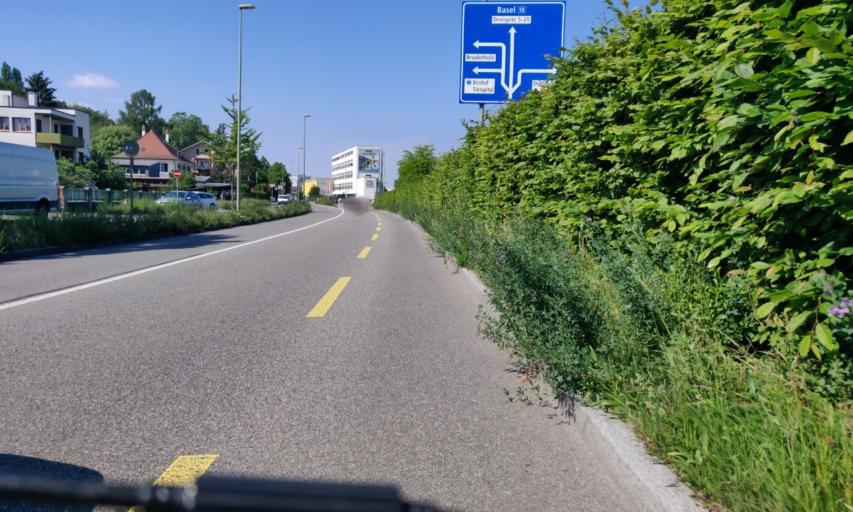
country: CH
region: Basel-Landschaft
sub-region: Bezirk Arlesheim
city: Munchenstein
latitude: 47.5282
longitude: 7.6057
